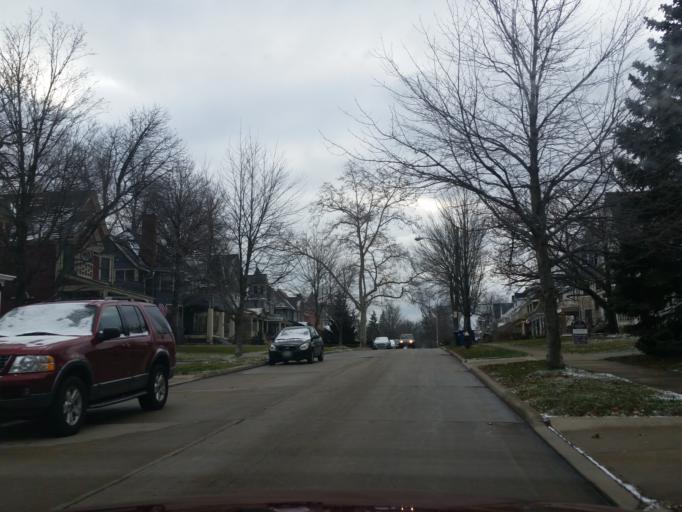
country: US
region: Ohio
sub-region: Cuyahoga County
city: Lakewood
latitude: 41.4834
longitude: -81.7804
